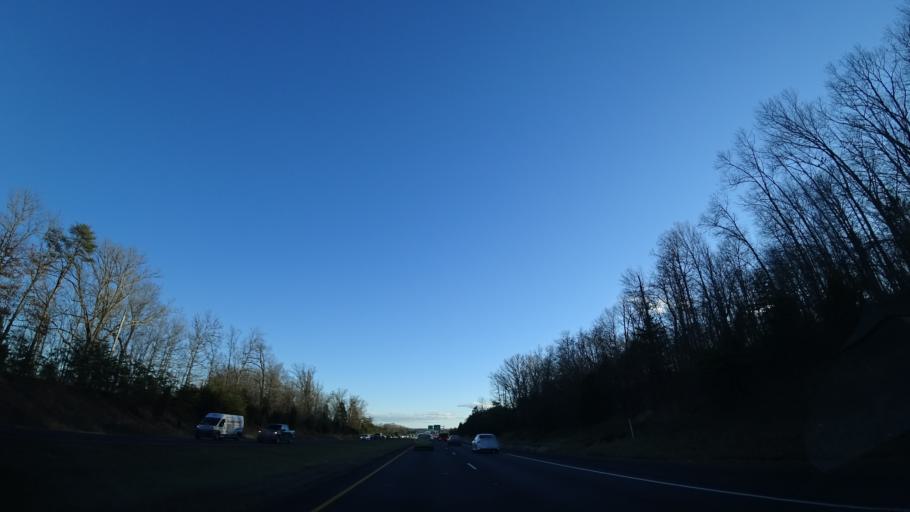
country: US
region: Virginia
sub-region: Prince William County
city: Bull Run
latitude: 38.7592
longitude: -77.5307
